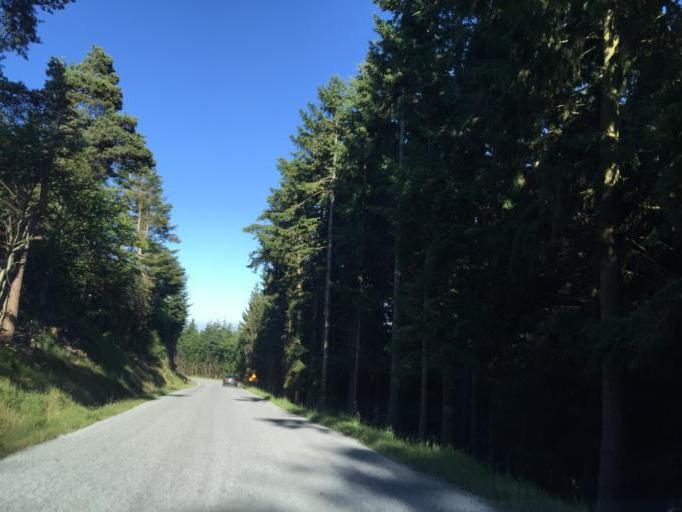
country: FR
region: Rhone-Alpes
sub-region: Departement de la Loire
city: Saint-Julien-Molin-Molette
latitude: 45.3336
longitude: 4.5844
